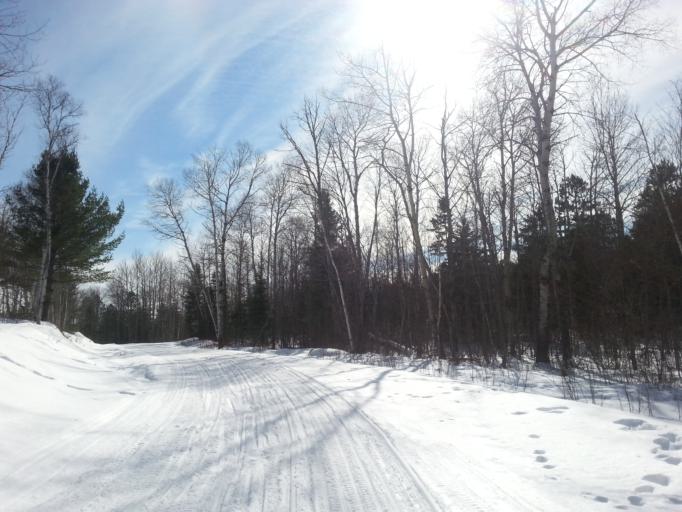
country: CA
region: Ontario
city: Greater Sudbury
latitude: 46.3331
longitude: -80.9062
